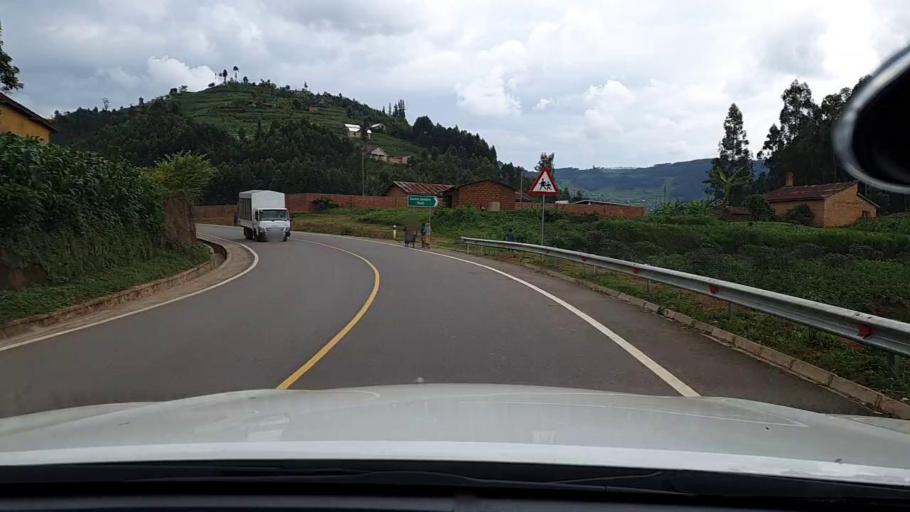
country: RW
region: Northern Province
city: Byumba
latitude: -1.6288
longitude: 29.9273
